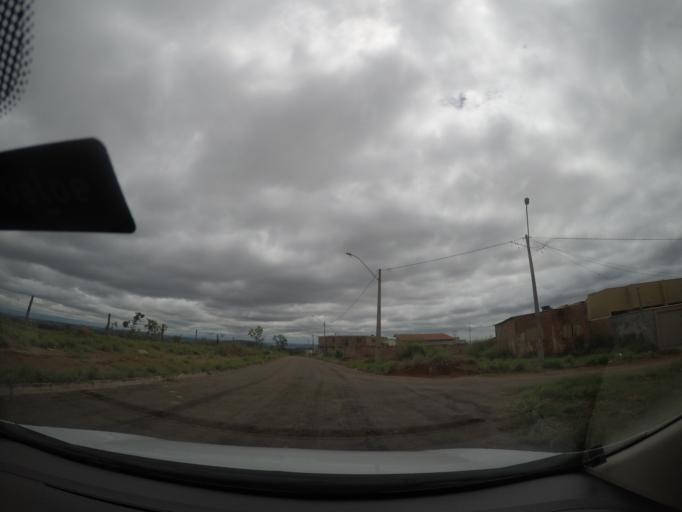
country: BR
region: Goias
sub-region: Trindade
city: Trindade
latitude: -16.7439
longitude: -49.3845
